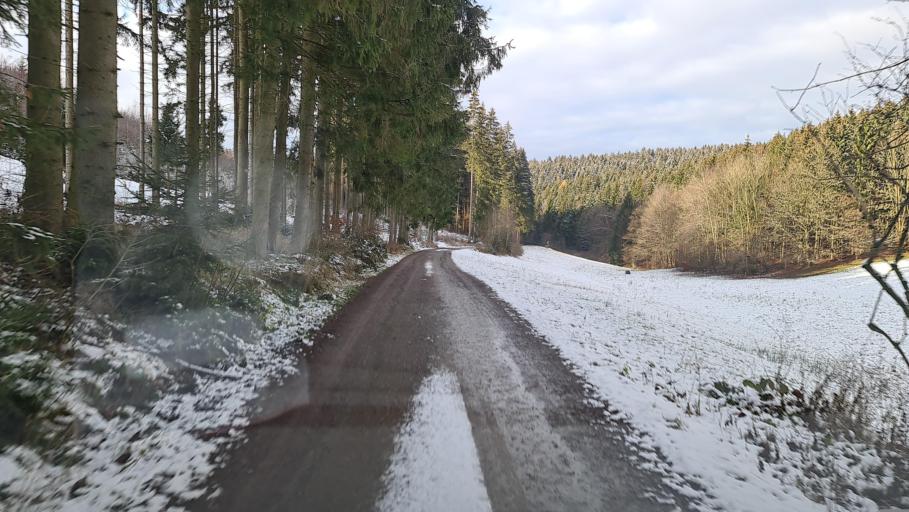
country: DE
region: Saxony
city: Dorfchemnitz
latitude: 50.7804
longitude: 13.4341
